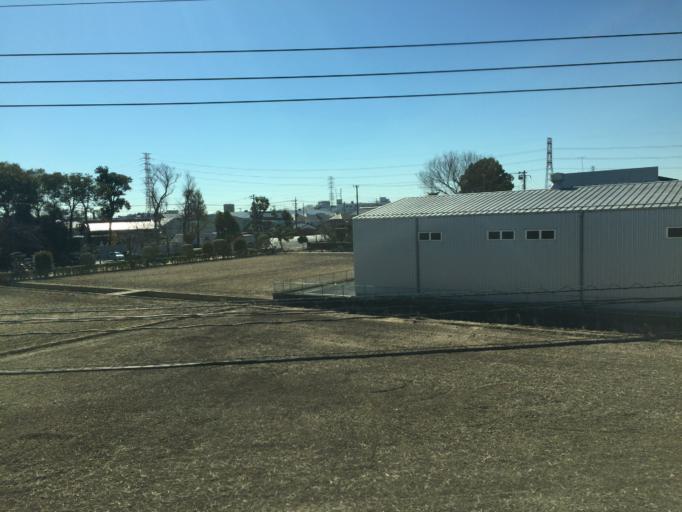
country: JP
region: Saitama
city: Shiki
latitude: 35.8344
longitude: 139.6014
